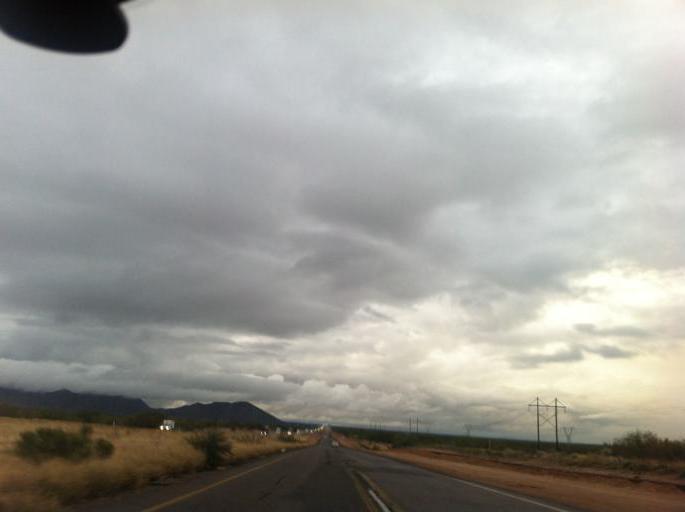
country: MX
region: Sonora
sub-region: San Miguel de Horcasitas
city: Las Mercedes [Agropecuaria]
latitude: 29.5427
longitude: -111.0111
